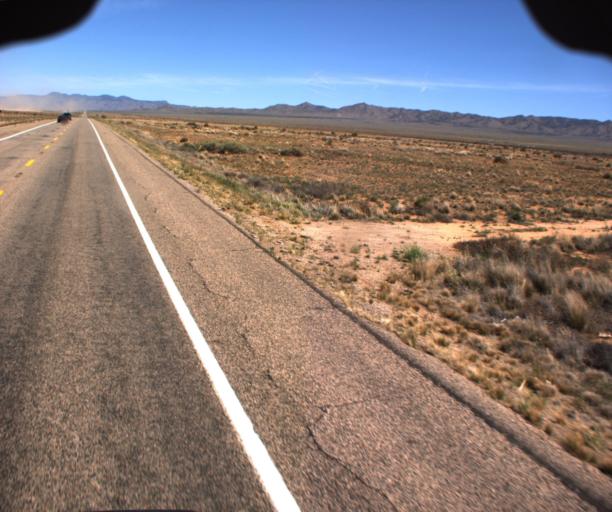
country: US
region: Arizona
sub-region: Mohave County
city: New Kingman-Butler
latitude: 35.3202
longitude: -113.9122
